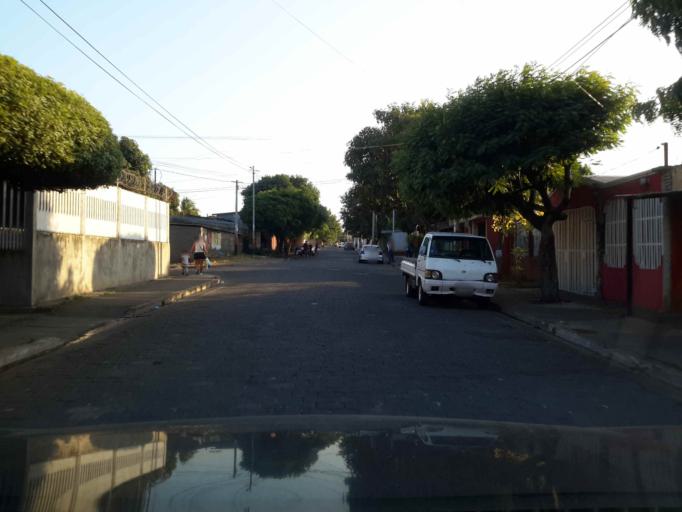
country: NI
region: Managua
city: Ciudad Sandino
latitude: 12.1524
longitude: -86.3029
